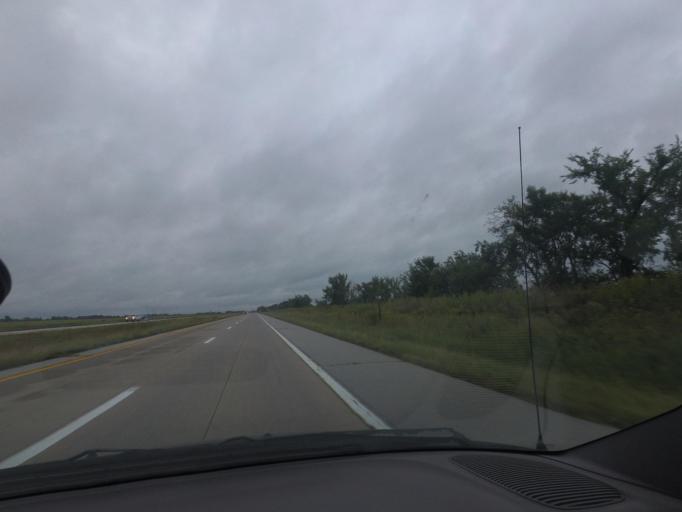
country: US
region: Missouri
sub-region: Marion County
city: Monroe City
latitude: 39.6625
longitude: -91.8340
